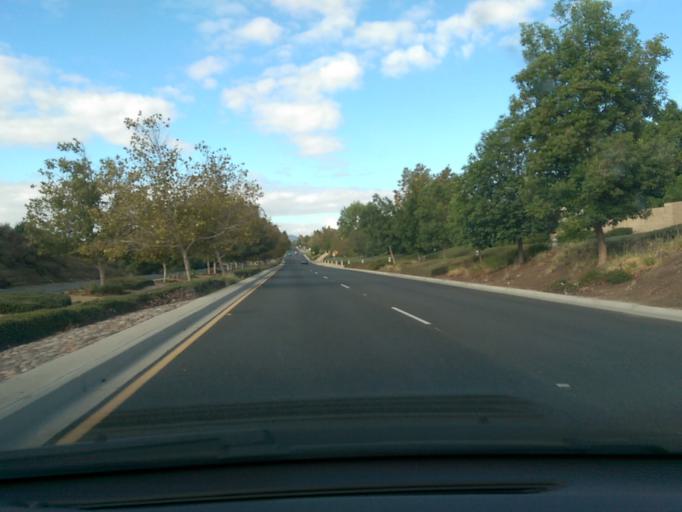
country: US
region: California
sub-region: Riverside County
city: Sunnyslope
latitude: 33.9835
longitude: -117.4359
